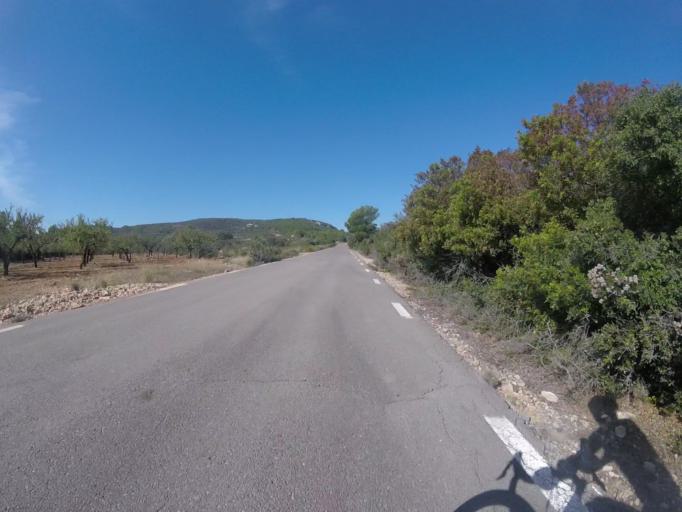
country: ES
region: Valencia
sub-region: Provincia de Castello
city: Sarratella
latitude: 40.2715
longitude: 0.0563
